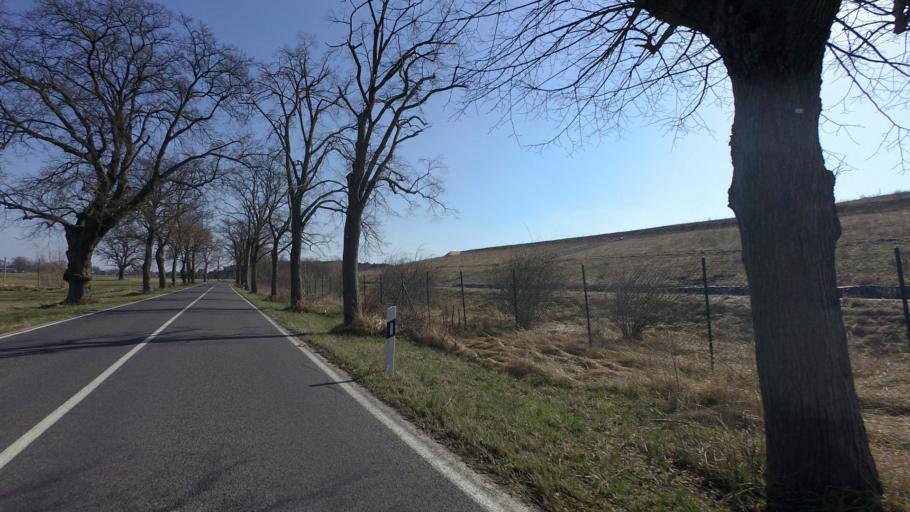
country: DE
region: Brandenburg
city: Leegebruch
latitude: 52.7548
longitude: 13.1649
